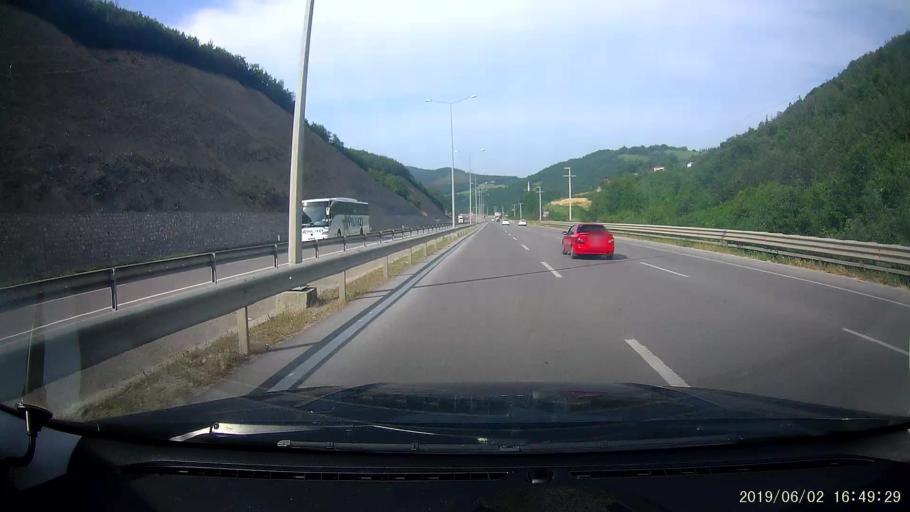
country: TR
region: Samsun
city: Samsun
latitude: 41.2383
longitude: 36.1629
